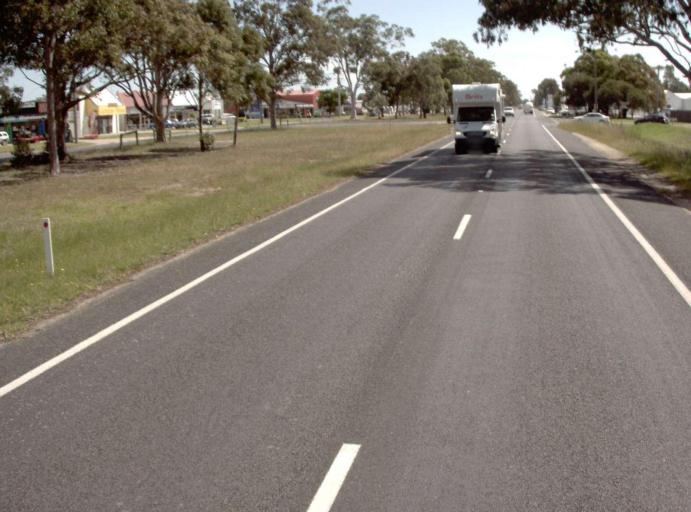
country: AU
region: Victoria
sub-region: East Gippsland
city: Bairnsdale
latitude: -37.8328
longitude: 147.6069
